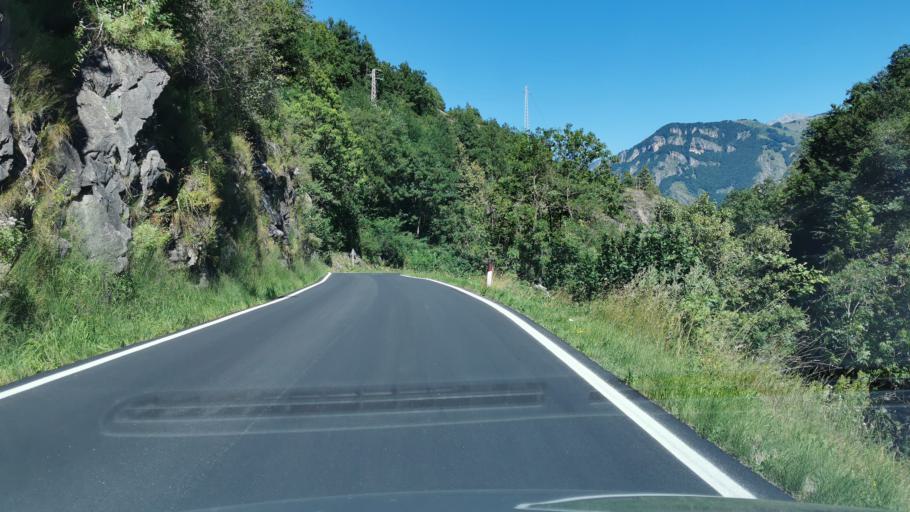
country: IT
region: Piedmont
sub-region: Provincia di Cuneo
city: Entracque
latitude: 44.2536
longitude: 7.3487
